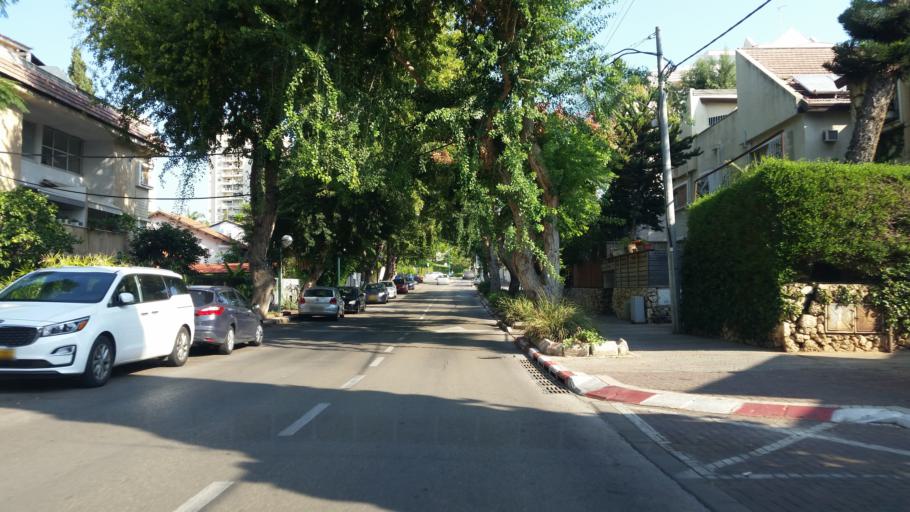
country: IL
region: Tel Aviv
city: Ramat HaSharon
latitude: 32.1486
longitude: 34.8461
